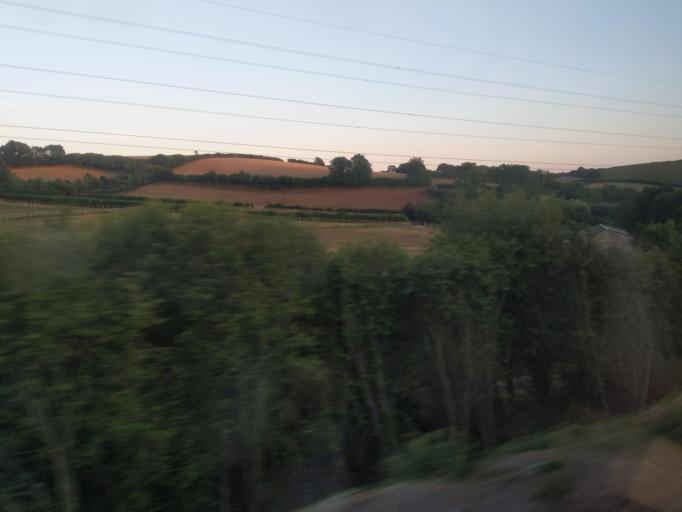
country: GB
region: England
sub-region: Devon
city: Ipplepen
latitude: 50.4788
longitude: -3.6334
